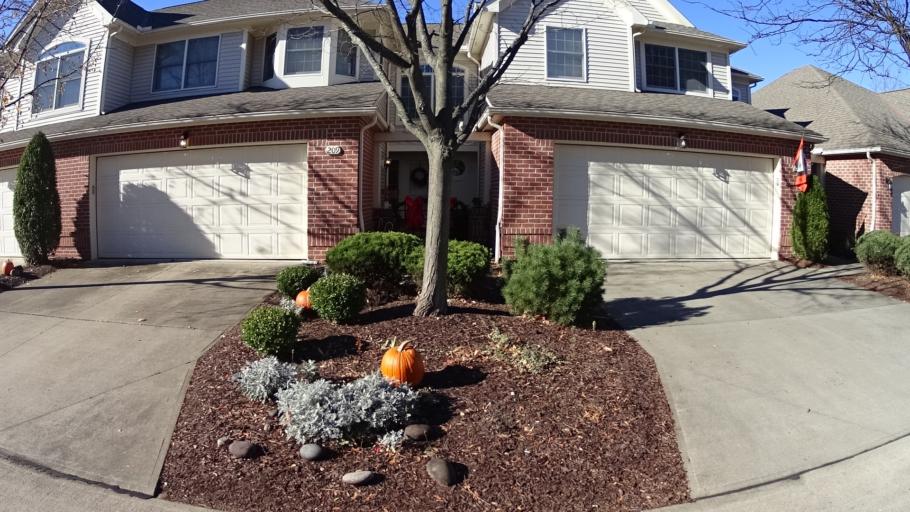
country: US
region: Ohio
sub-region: Lorain County
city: Avon Lake
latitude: 41.4952
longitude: -81.9759
